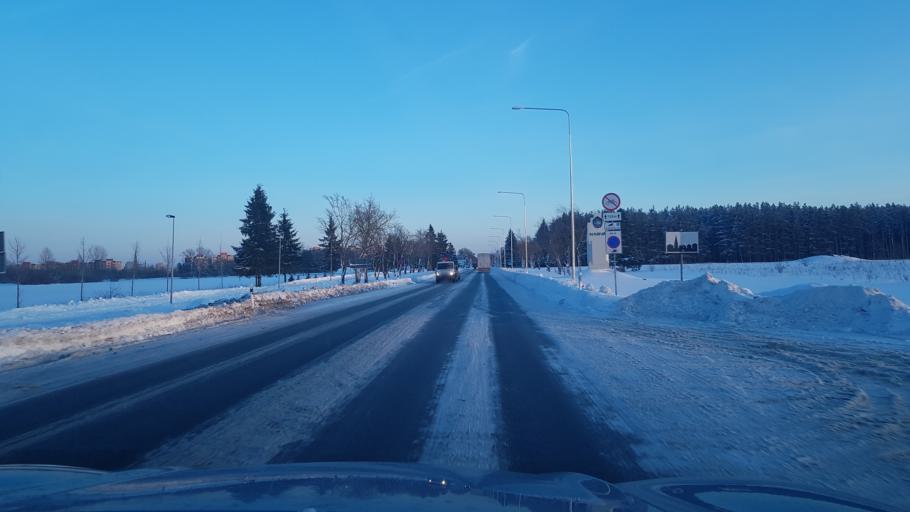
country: EE
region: Ida-Virumaa
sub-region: Narva linn
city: Narva
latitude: 59.3867
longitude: 28.1481
